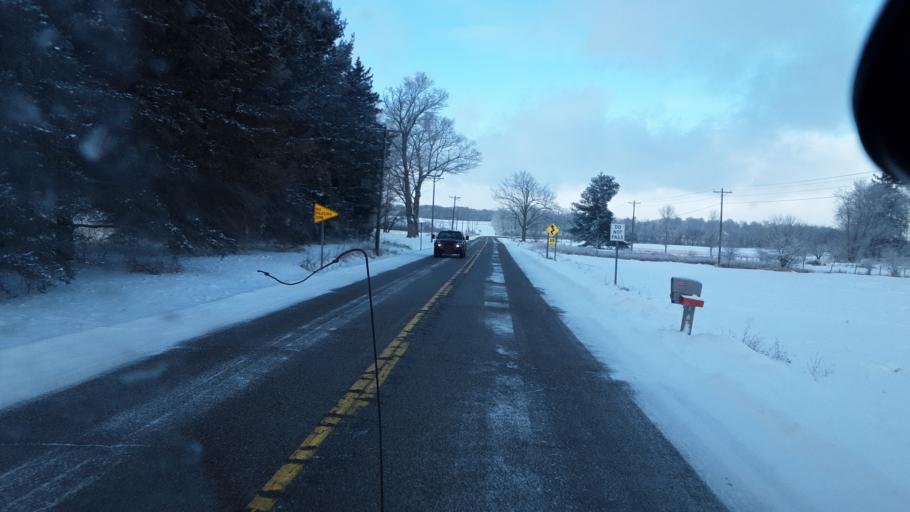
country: US
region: Michigan
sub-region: Eaton County
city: Eaton Rapids
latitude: 42.4875
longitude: -84.6159
